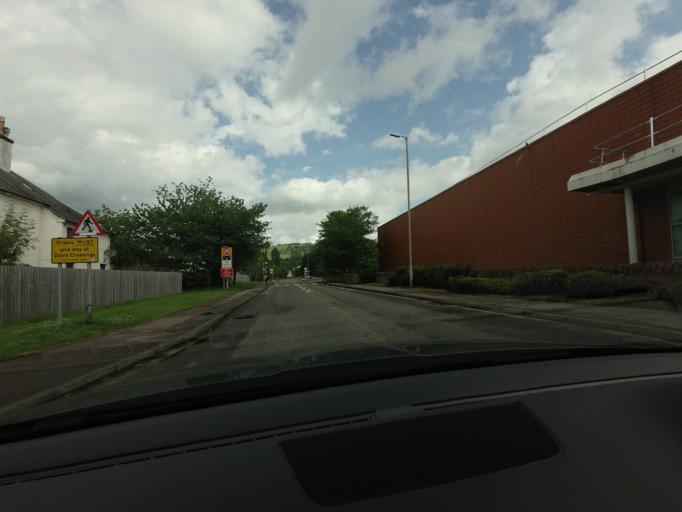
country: GB
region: Scotland
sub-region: Highland
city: Dingwall
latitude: 57.5975
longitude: -4.4317
